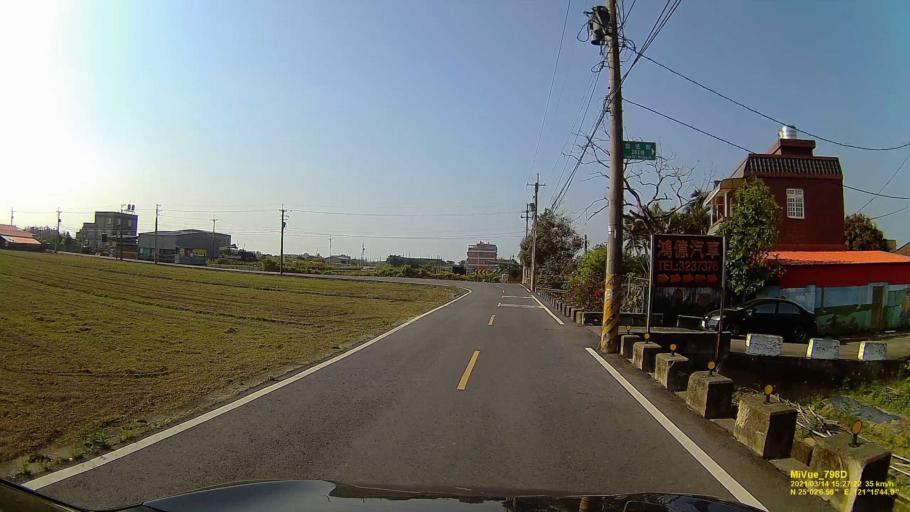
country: TW
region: Taiwan
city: Taoyuan City
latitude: 25.0351
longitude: 121.2624
